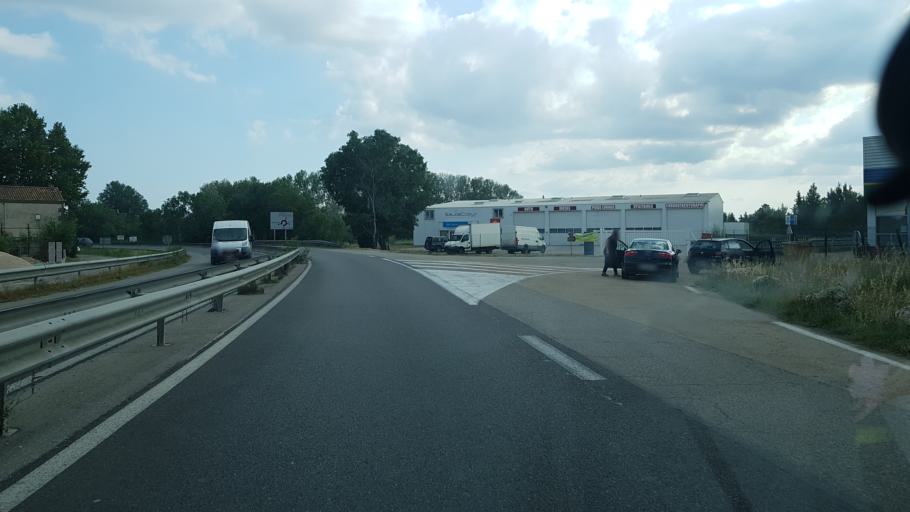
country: FR
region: Languedoc-Roussillon
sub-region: Departement du Gard
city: Fourques
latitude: 43.6773
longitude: 4.6067
